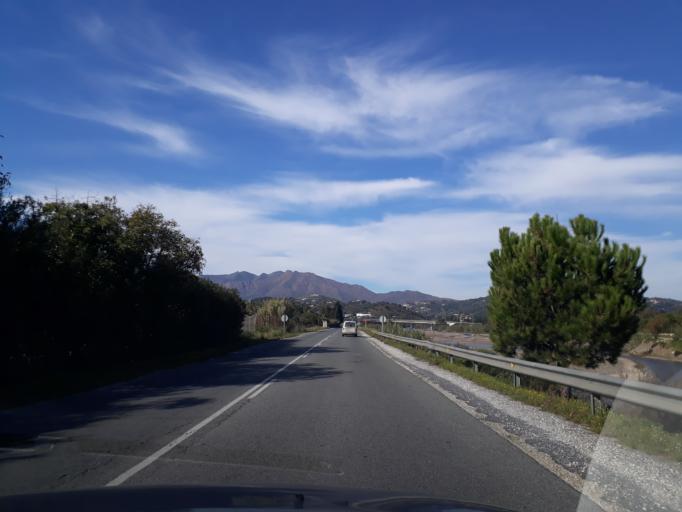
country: ES
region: Andalusia
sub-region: Provincia de Malaga
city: Fuengirola
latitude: 36.5469
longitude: -4.6897
